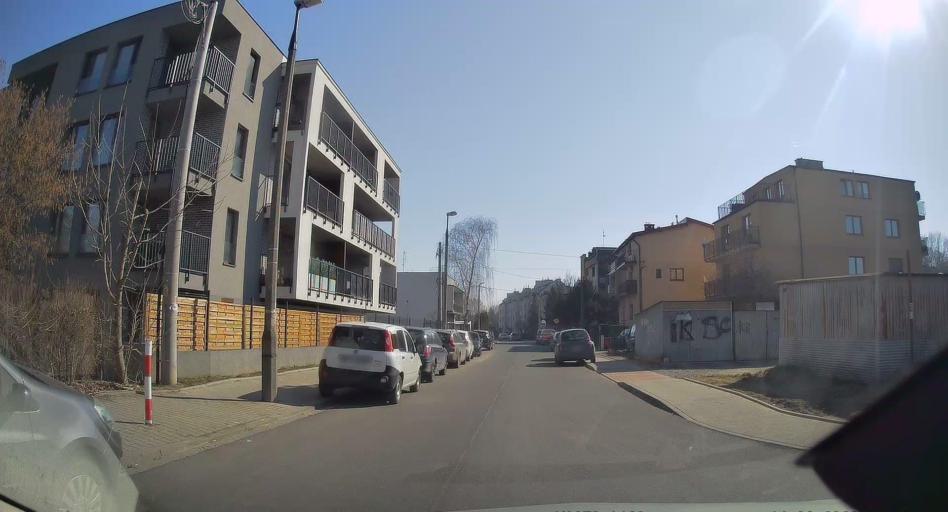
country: PL
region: Lesser Poland Voivodeship
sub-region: Krakow
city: Krakow
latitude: 50.0221
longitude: 19.9941
